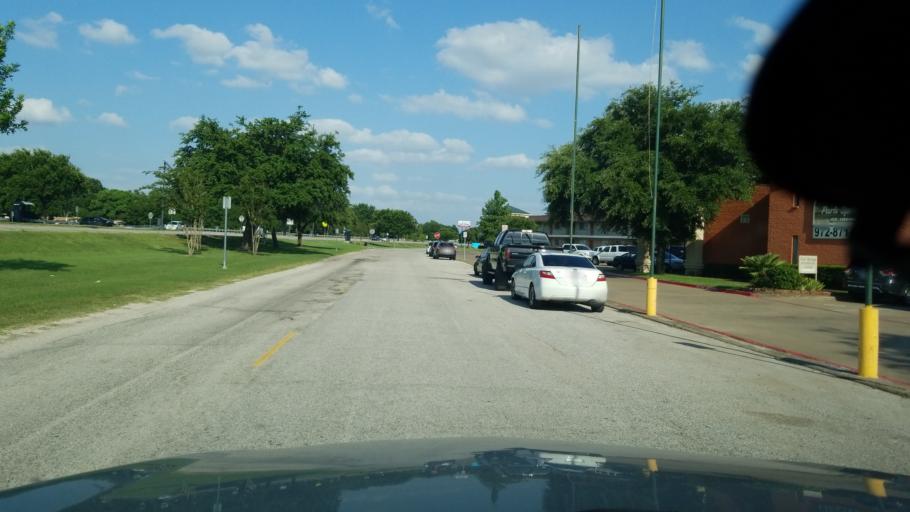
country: US
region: Texas
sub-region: Dallas County
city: Irving
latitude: 32.8264
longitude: -96.9714
